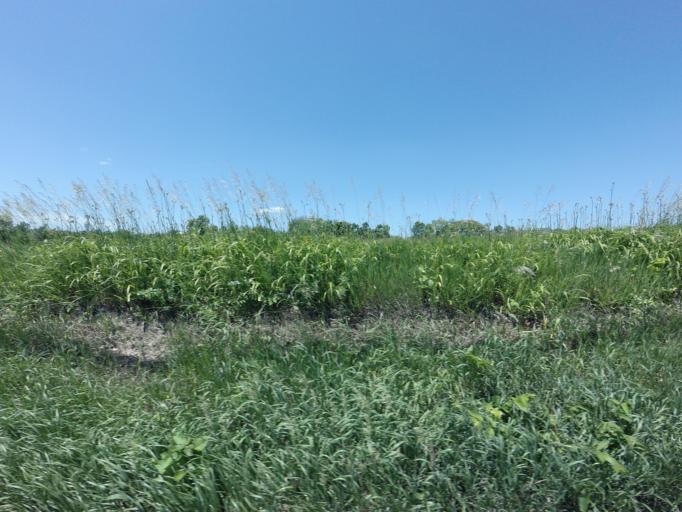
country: US
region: West Virginia
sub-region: Jefferson County
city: Ranson
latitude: 39.3236
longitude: -77.8361
